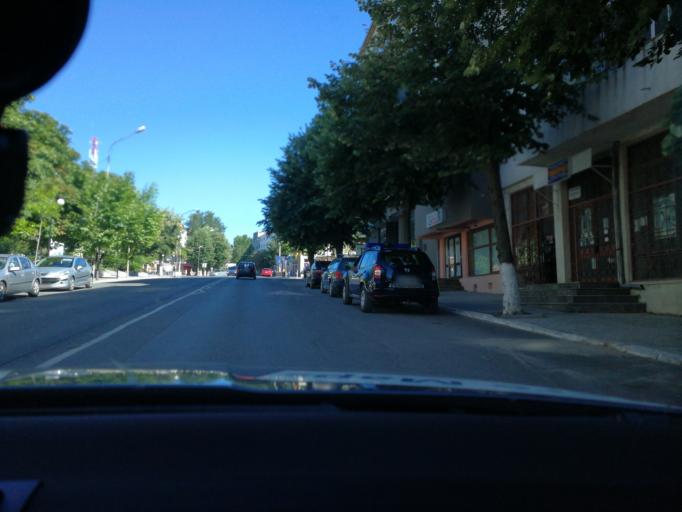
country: RO
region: Tulcea
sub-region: Oras Macin
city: Macin
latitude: 45.2460
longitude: 28.1295
